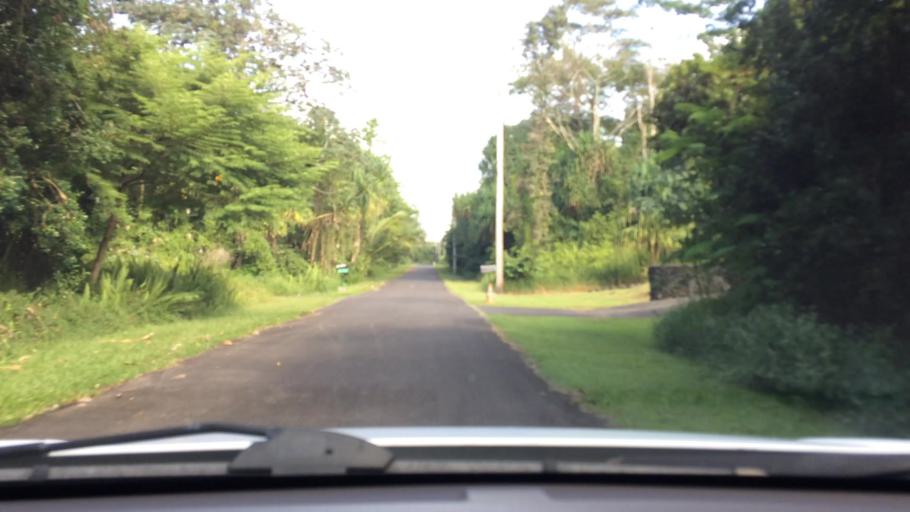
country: US
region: Hawaii
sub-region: Hawaii County
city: Hawaiian Beaches
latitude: 19.5455
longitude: -154.9001
